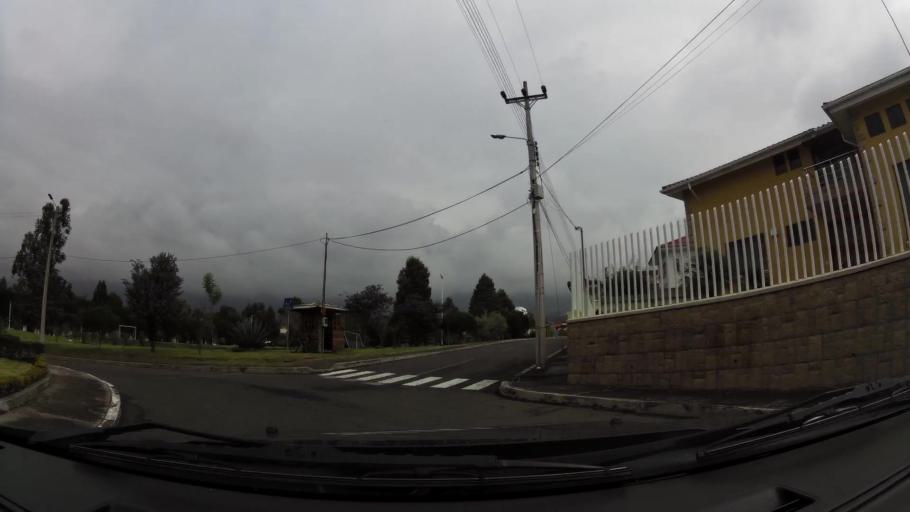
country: EC
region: Pichincha
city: Sangolqui
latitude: -0.3044
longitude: -78.4797
